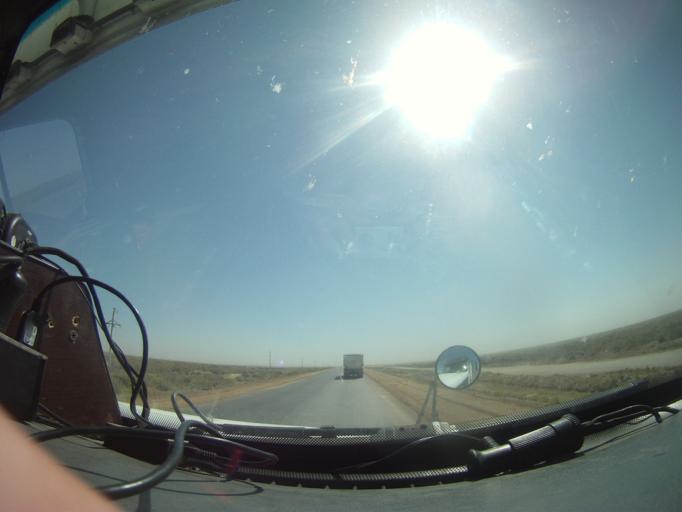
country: KZ
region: Qyzylorda
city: Dzhalagash
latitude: 45.0368
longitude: 64.4054
